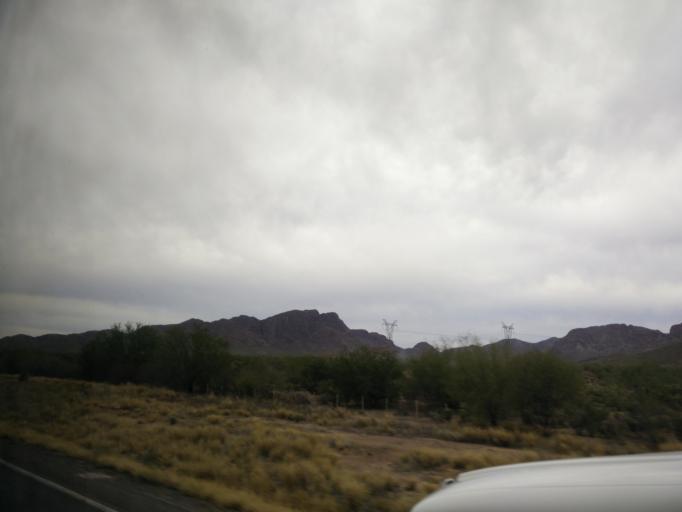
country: MX
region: Sonora
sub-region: Hermosillo
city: Miguel Aleman (La Doce)
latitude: 28.5786
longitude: -111.0291
